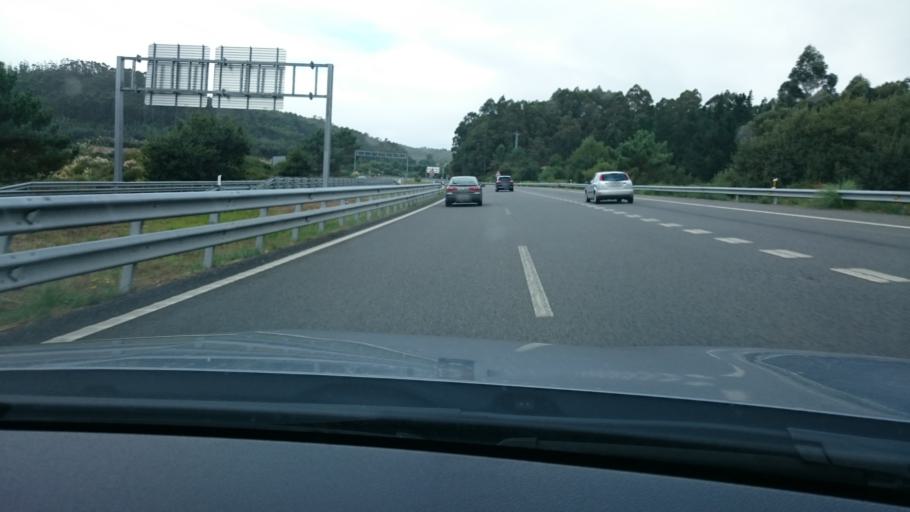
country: ES
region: Galicia
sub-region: Provincia da Coruna
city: Culleredo
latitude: 43.2759
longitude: -8.4088
